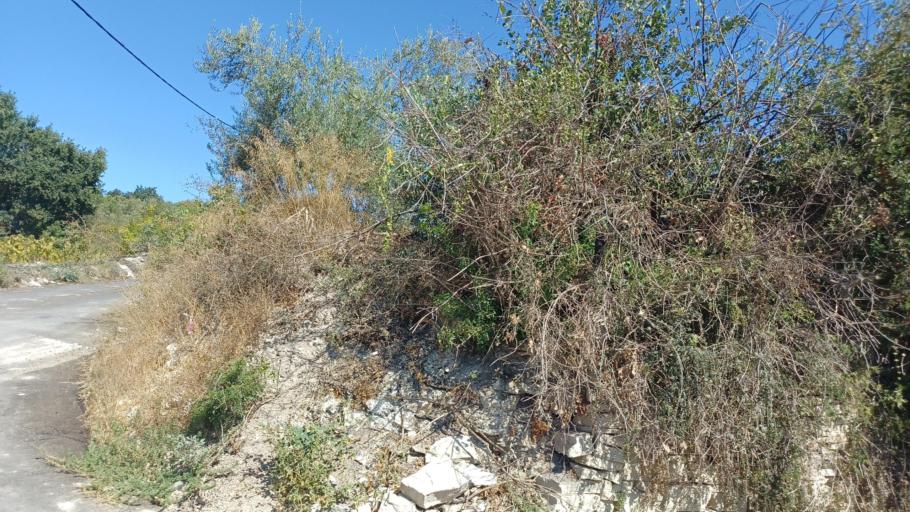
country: CY
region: Pafos
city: Mesogi
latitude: 34.8536
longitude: 32.5111
